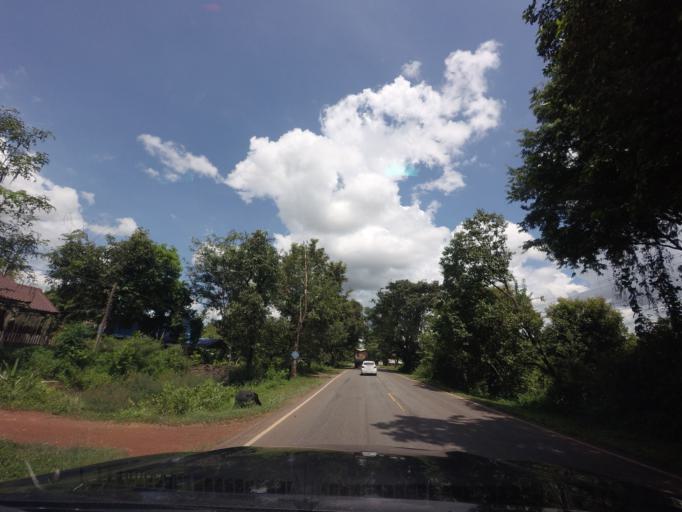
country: TH
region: Changwat Udon Thani
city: Phibun Rak
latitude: 17.5884
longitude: 103.0475
